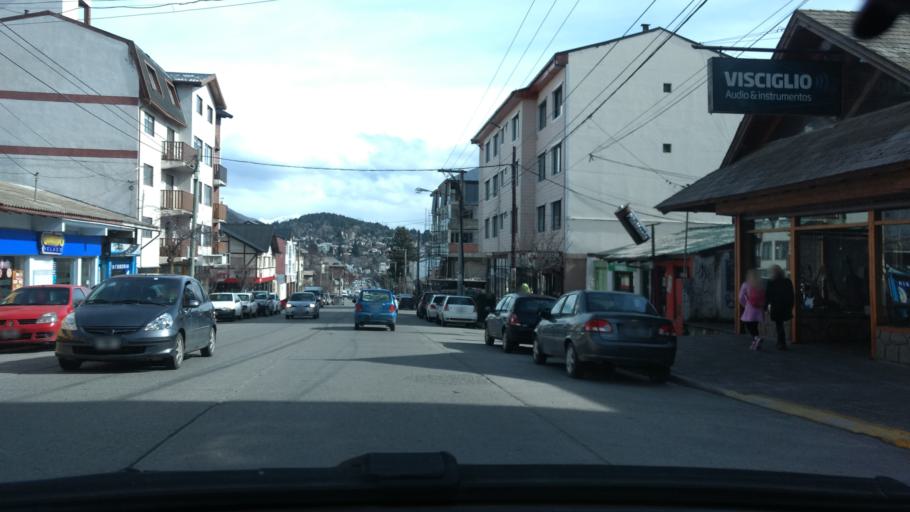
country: AR
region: Rio Negro
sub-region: Departamento de Bariloche
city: San Carlos de Bariloche
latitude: -41.1377
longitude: -71.3010
